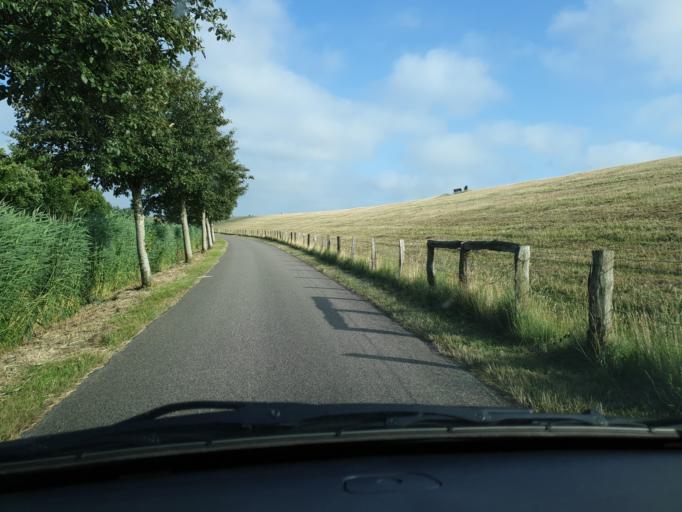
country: DE
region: Schleswig-Holstein
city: Friedrichskoog
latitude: 54.0256
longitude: 8.8395
